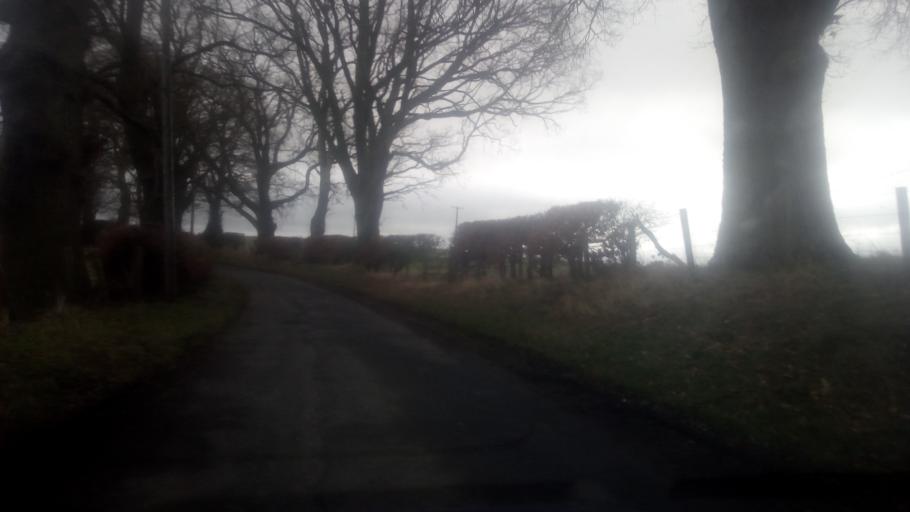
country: GB
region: Scotland
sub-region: The Scottish Borders
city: Jedburgh
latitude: 55.5291
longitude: -2.5097
